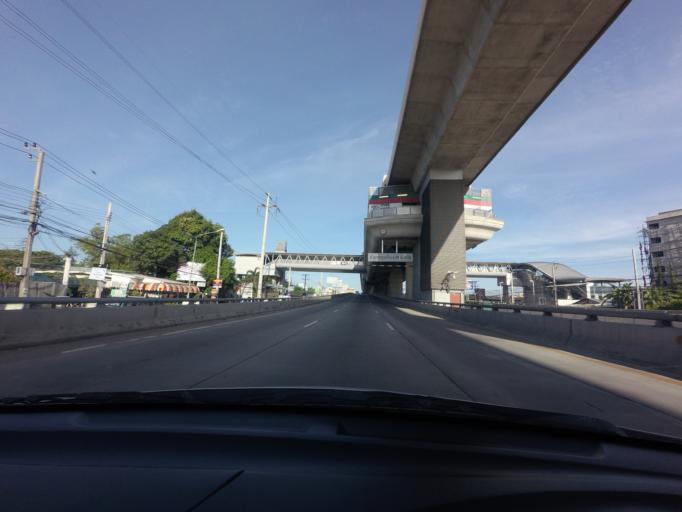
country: TH
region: Nonthaburi
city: Bang Bua Thong
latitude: 13.8759
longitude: 100.4362
